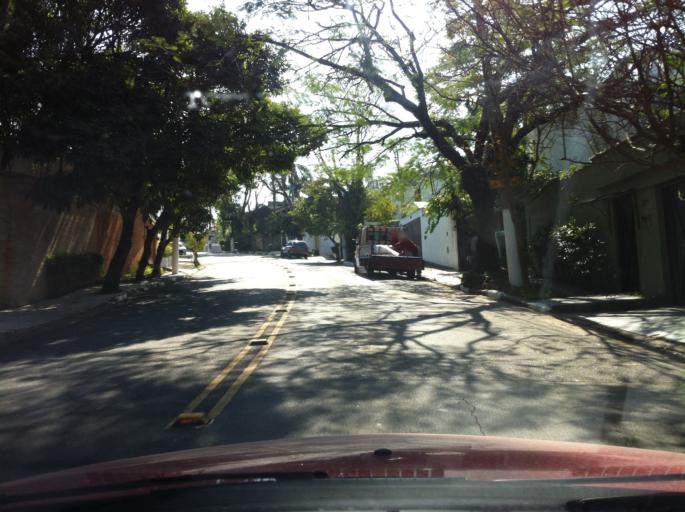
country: BR
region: Sao Paulo
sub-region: Diadema
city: Diadema
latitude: -23.6373
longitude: -46.6892
